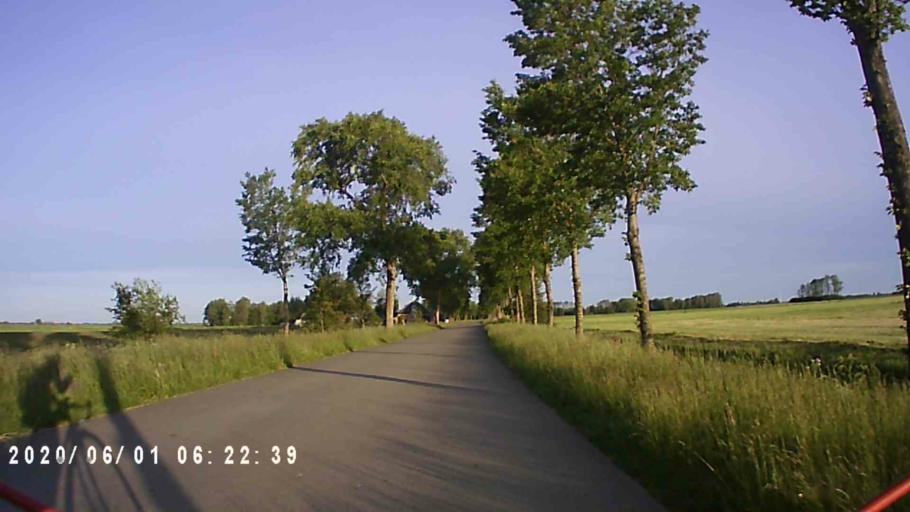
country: NL
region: Friesland
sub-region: Gemeente Kollumerland en Nieuwkruisland
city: Kollum
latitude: 53.2650
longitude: 6.2216
